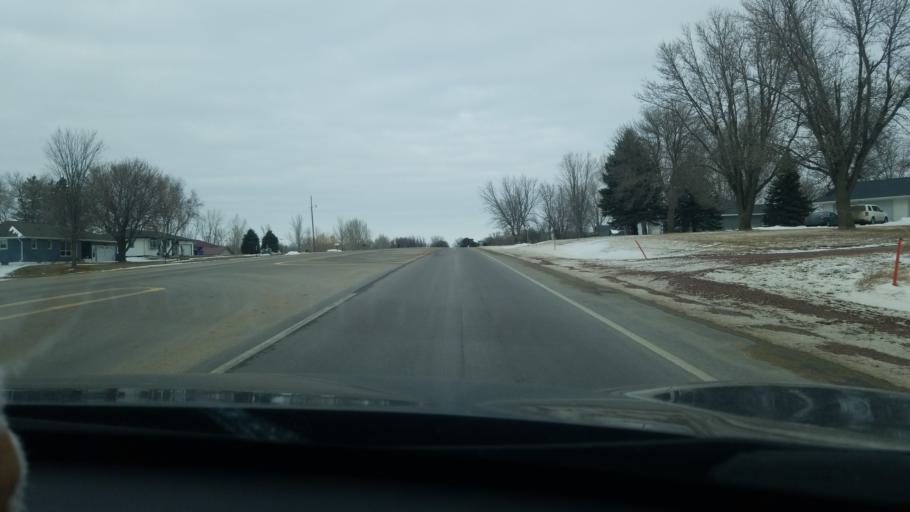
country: US
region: South Dakota
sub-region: Minnehaha County
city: Brandon
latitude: 43.4472
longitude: -96.4295
